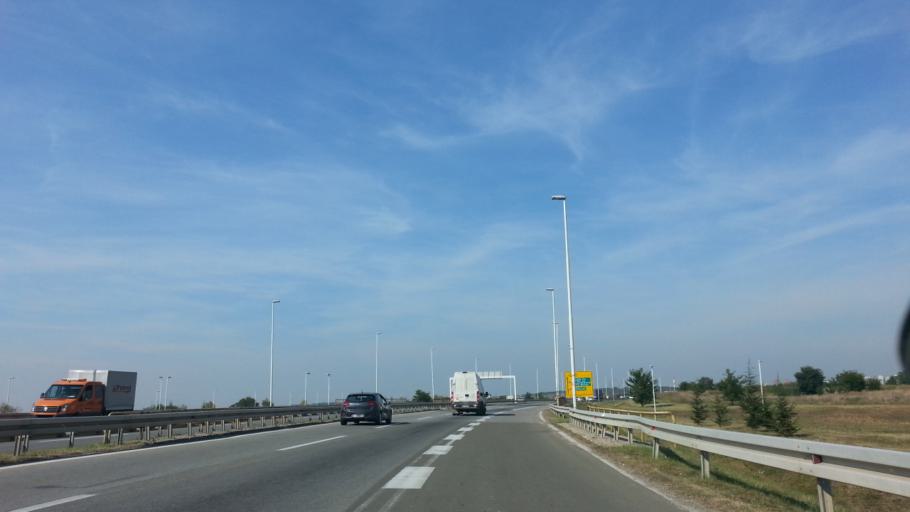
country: RS
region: Central Serbia
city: Sremcica
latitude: 44.7019
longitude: 20.4133
